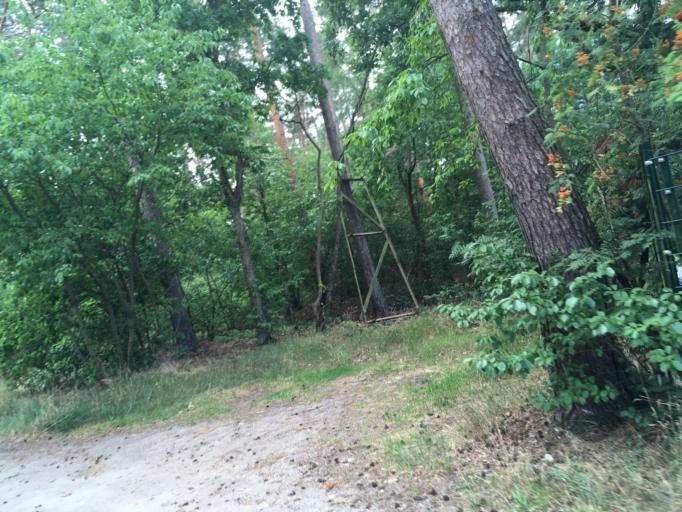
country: DE
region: Lower Saxony
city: Neu Darchau
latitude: 53.2867
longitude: 10.9451
